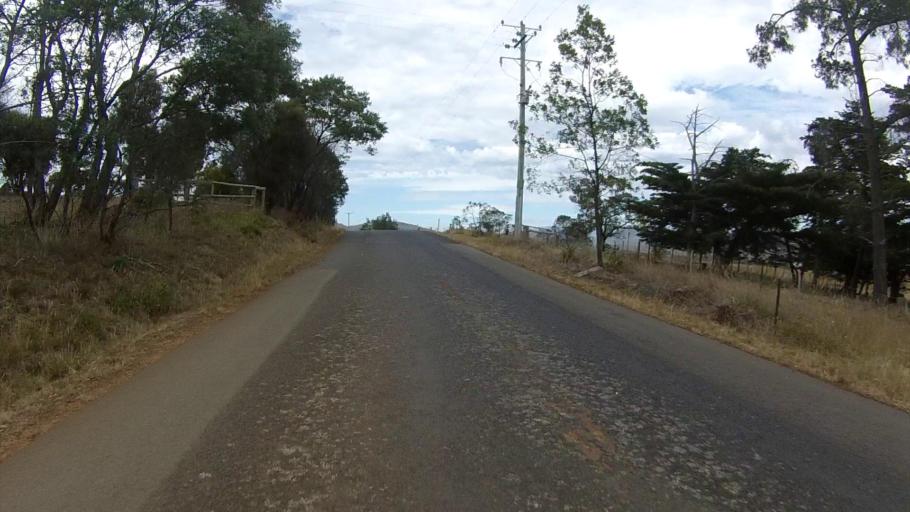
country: AU
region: Tasmania
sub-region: Clarence
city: Cambridge
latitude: -42.7141
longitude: 147.4531
